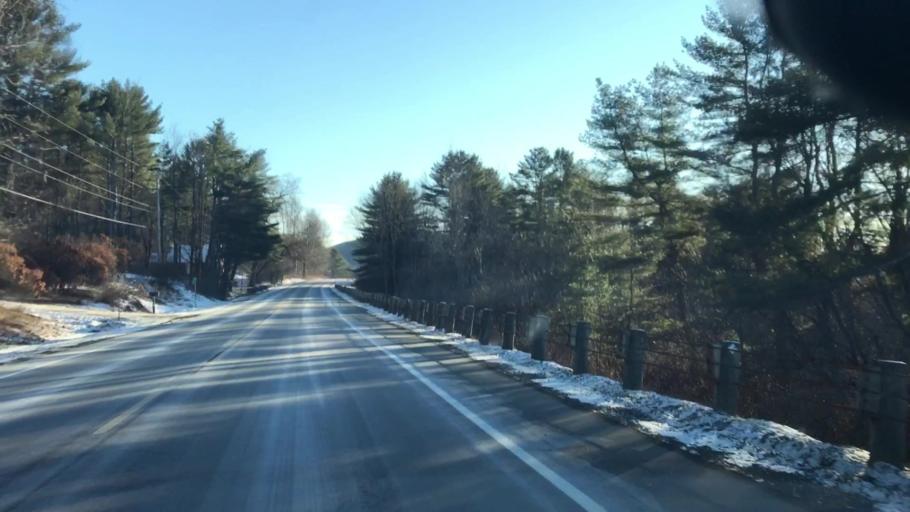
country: US
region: New Hampshire
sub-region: Grafton County
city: Lyme Town Offices
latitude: 43.8583
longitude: -72.1553
